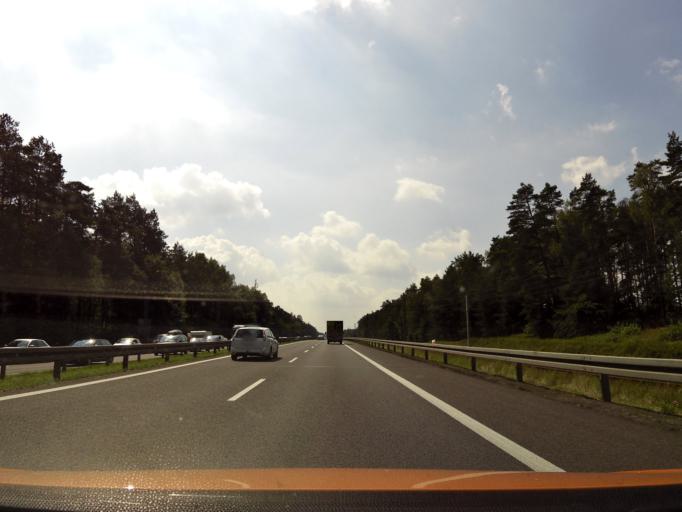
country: PL
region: West Pomeranian Voivodeship
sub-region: Powiat goleniowski
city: Goleniow
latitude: 53.5059
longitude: 14.8007
